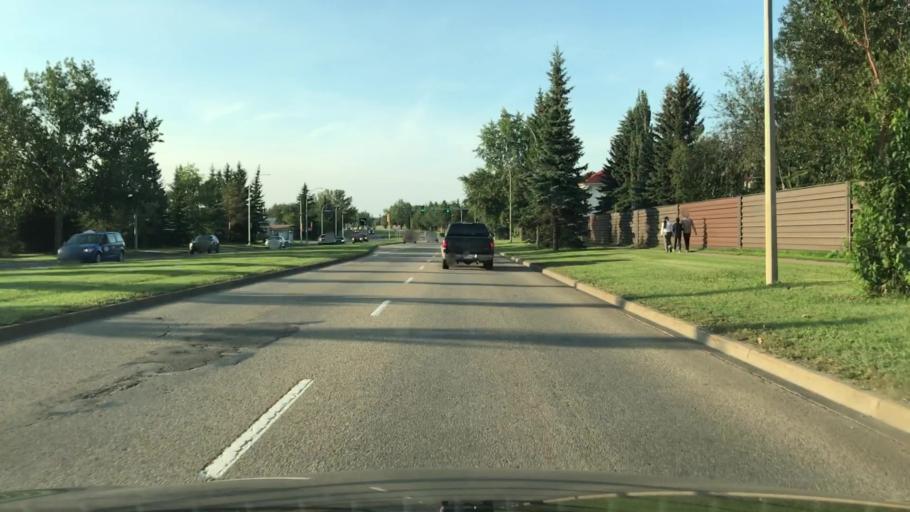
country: CA
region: Alberta
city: Beaumont
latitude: 53.4483
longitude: -113.4193
